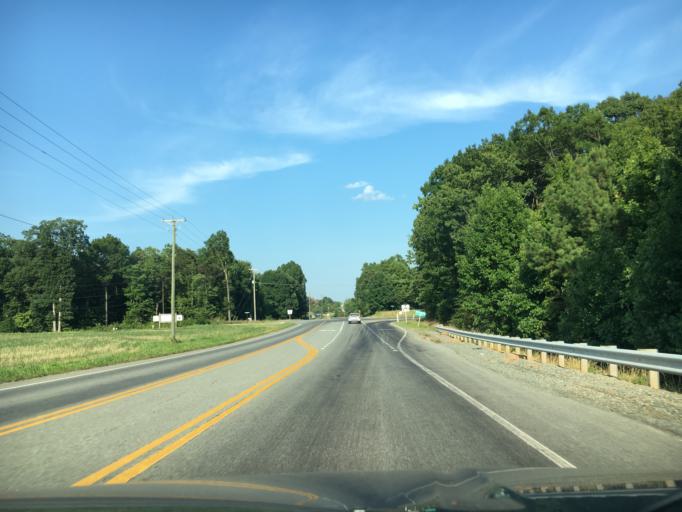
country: US
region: Virginia
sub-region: Franklin County
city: Union Hall
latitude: 36.9932
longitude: -79.7158
